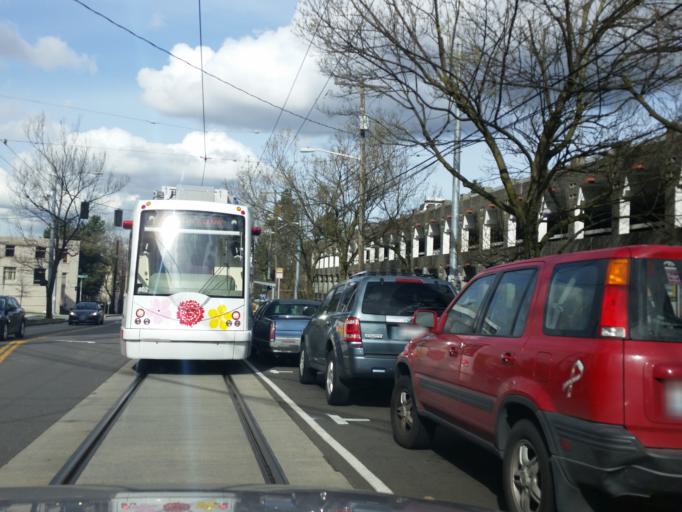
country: US
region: Washington
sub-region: King County
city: Seattle
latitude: 47.6095
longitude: -122.3207
